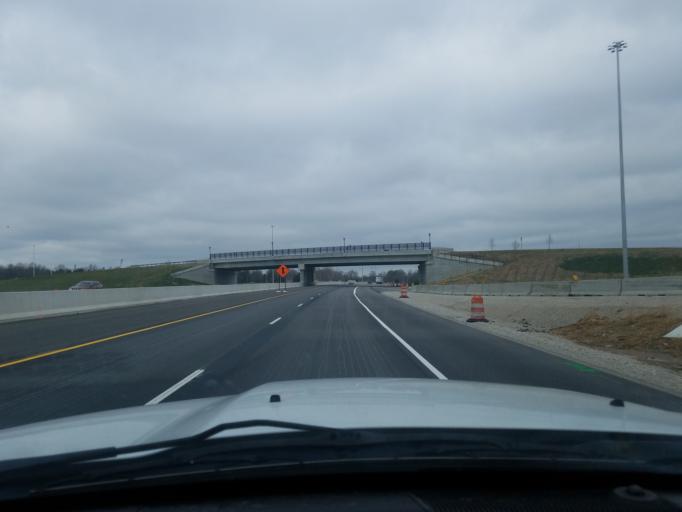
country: US
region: Indiana
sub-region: Monroe County
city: Bloomington
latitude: 39.1213
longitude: -86.5702
